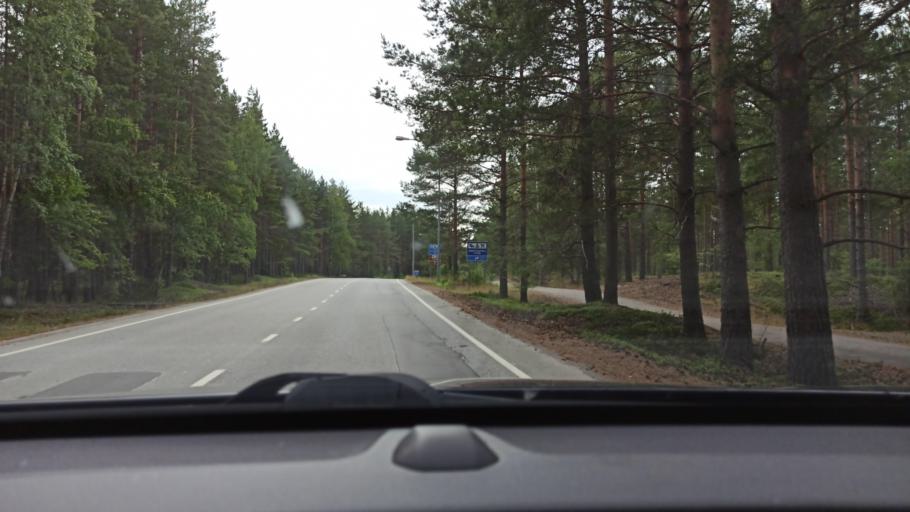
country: FI
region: Satakunta
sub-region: Pori
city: Luvia
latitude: 61.5725
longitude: 21.5370
